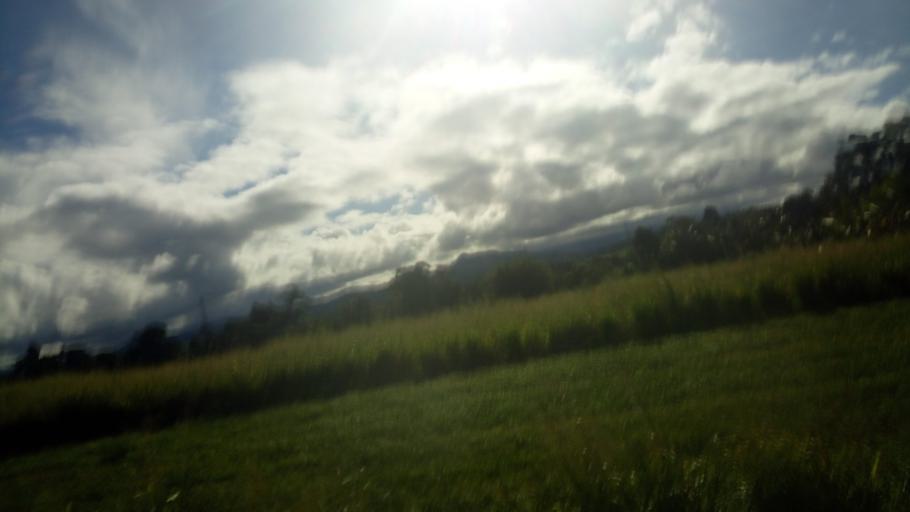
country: AU
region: Queensland
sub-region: Cassowary Coast
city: Innisfail
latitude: -17.5284
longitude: 145.9806
